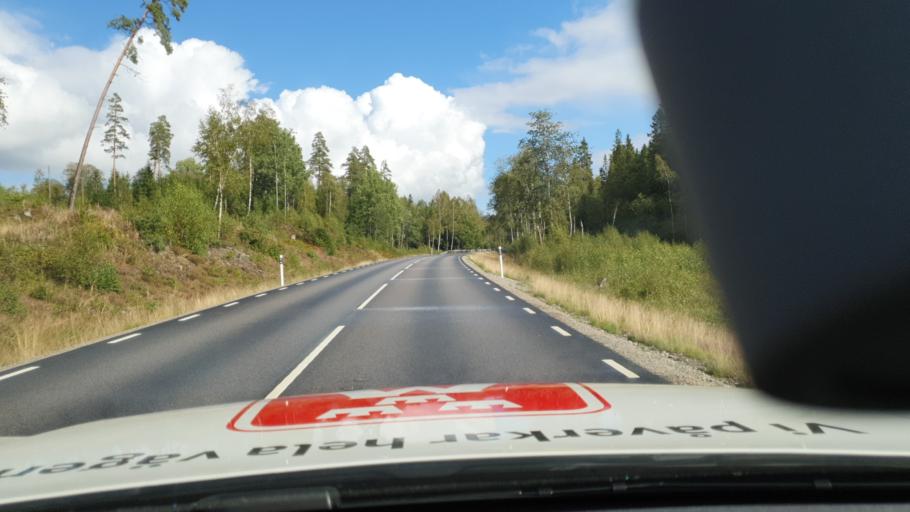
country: SE
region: Vaestra Goetaland
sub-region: Boras Kommun
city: Sandared
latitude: 57.7885
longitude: 12.7411
